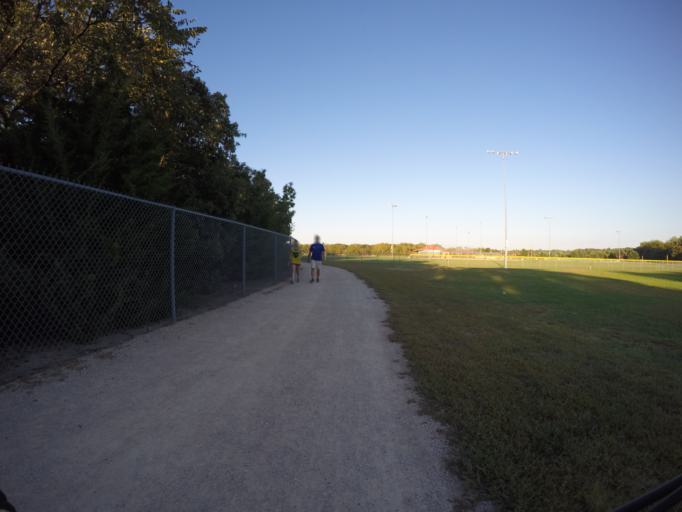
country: US
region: Kansas
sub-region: Riley County
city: Manhattan
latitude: 39.1833
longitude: -96.6343
